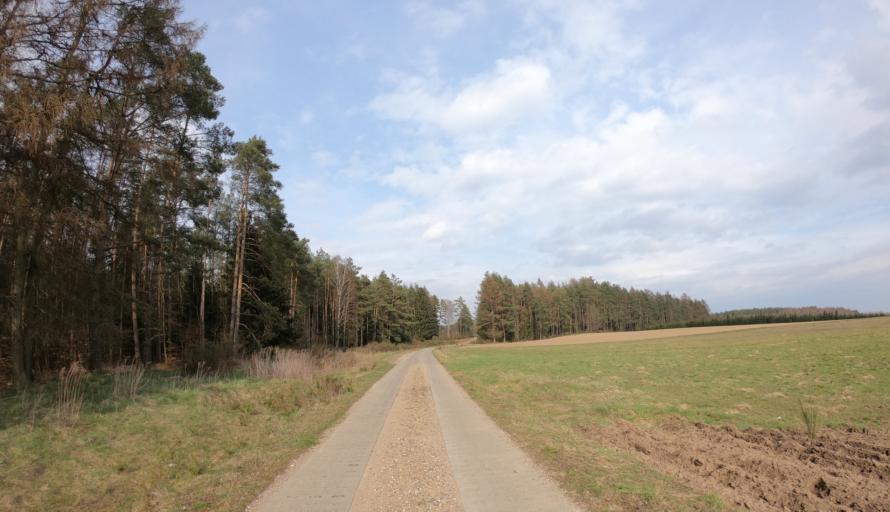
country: PL
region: West Pomeranian Voivodeship
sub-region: Powiat swidwinski
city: Rabino
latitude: 53.8447
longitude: 15.8494
